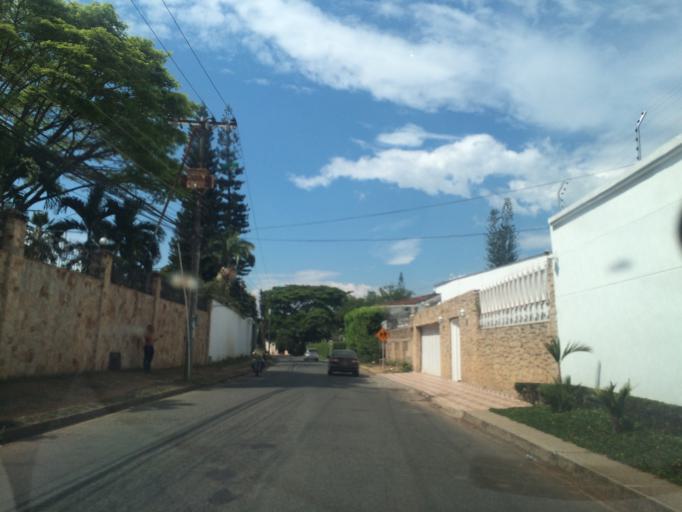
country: CO
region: Valle del Cauca
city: Cali
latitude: 3.3595
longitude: -76.5327
